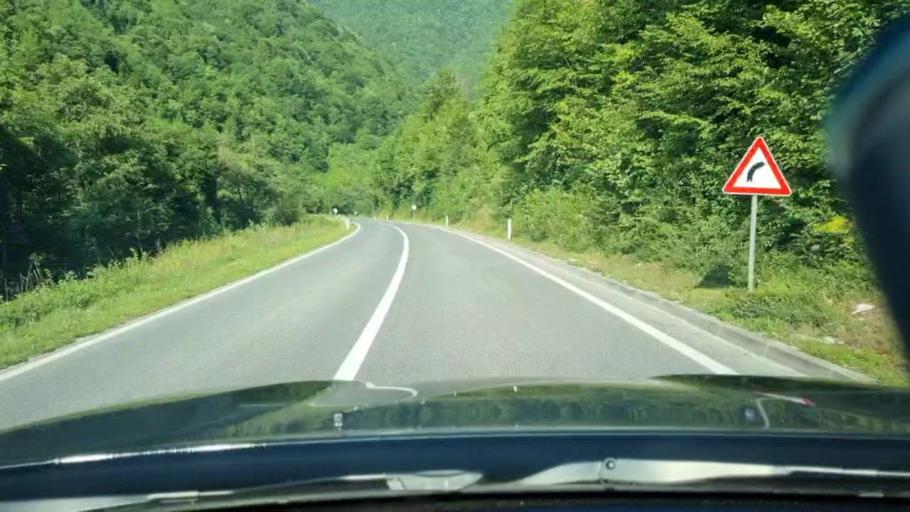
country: BA
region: Federation of Bosnia and Herzegovina
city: Donji Vakuf
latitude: 44.2104
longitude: 17.3255
